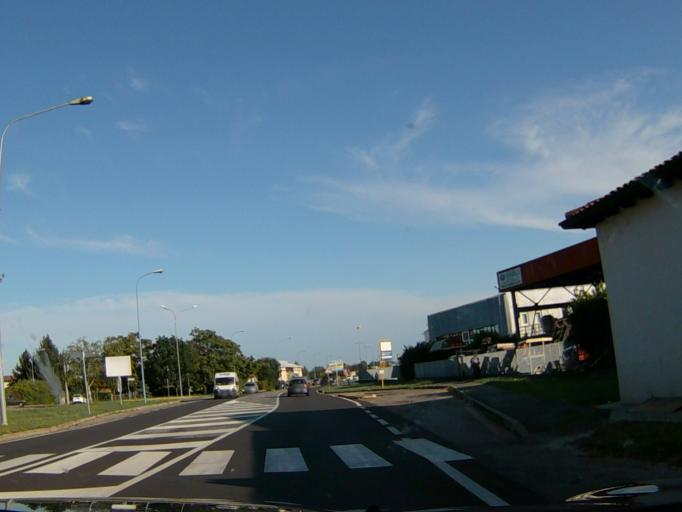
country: IT
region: Lombardy
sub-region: Provincia di Brescia
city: Molinetto
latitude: 45.4923
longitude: 10.3619
